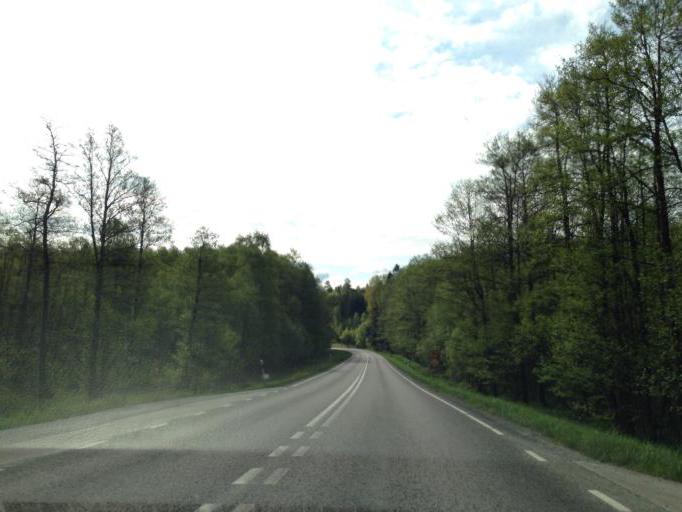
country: SE
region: Soedermanland
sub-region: Nykopings Kommun
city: Stigtomta
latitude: 58.9744
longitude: 16.8372
